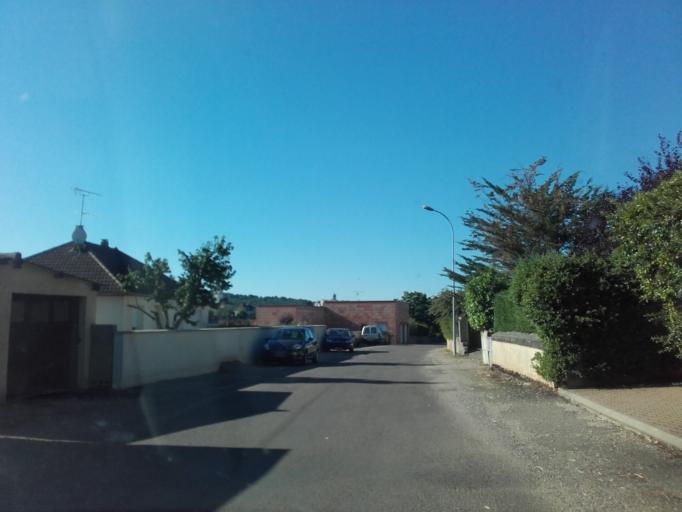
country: FR
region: Bourgogne
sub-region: Departement de Saone-et-Loire
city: Rully
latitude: 46.8690
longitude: 4.7420
